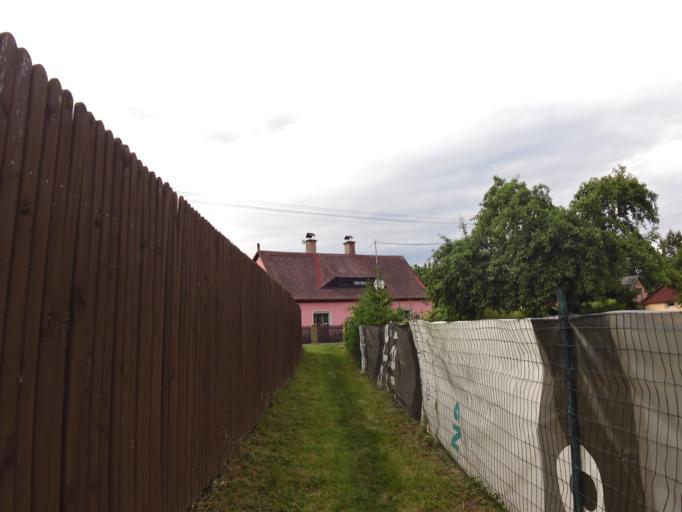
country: CZ
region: Ustecky
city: Varnsdorf
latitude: 50.8961
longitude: 14.6173
